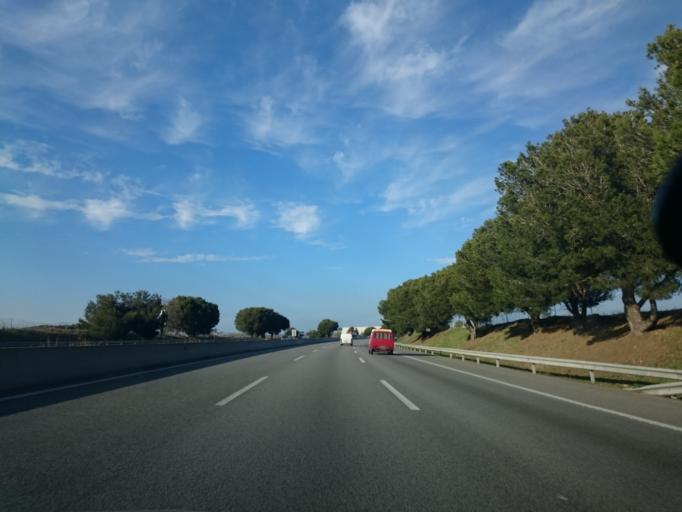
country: ES
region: Catalonia
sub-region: Provincia de Barcelona
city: La Granada
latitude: 41.3652
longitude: 1.7259
